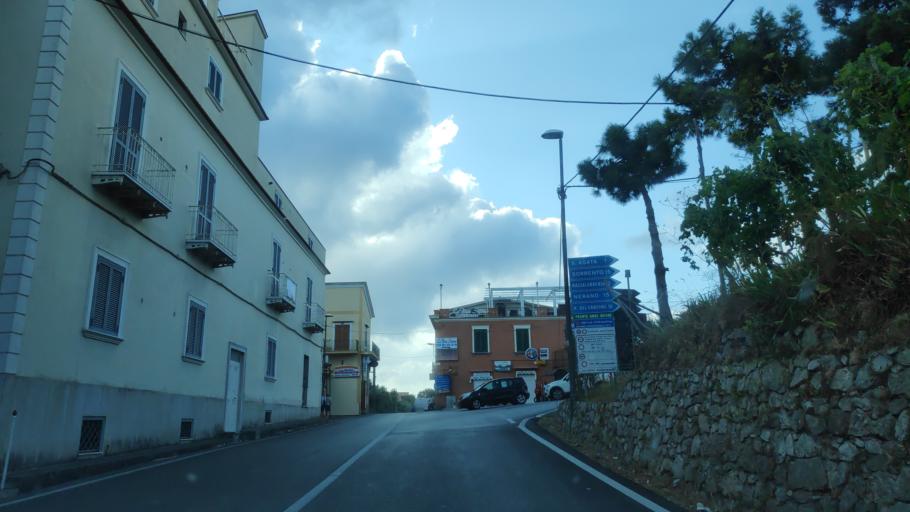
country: IT
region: Campania
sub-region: Provincia di Napoli
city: Piano di Sorrento
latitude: 40.6177
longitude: 14.4271
